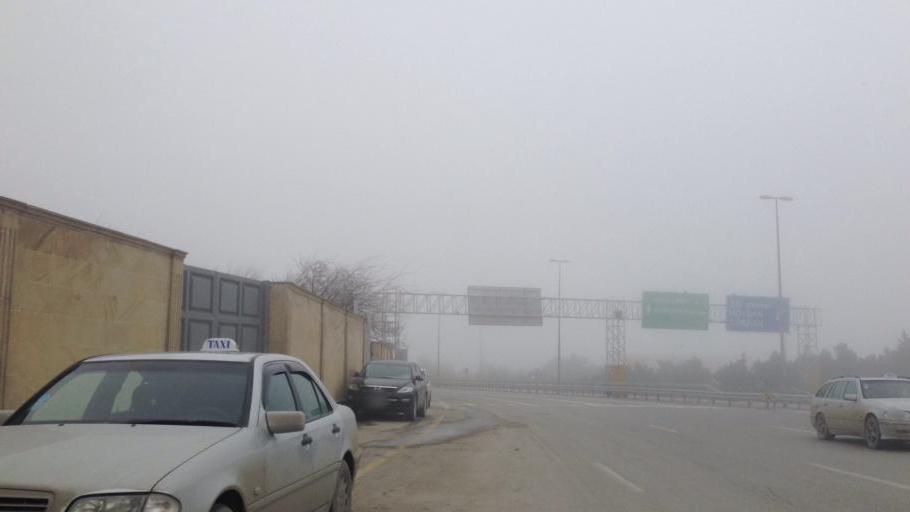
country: AZ
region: Baki
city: Qaracuxur
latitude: 40.3486
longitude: 49.9619
